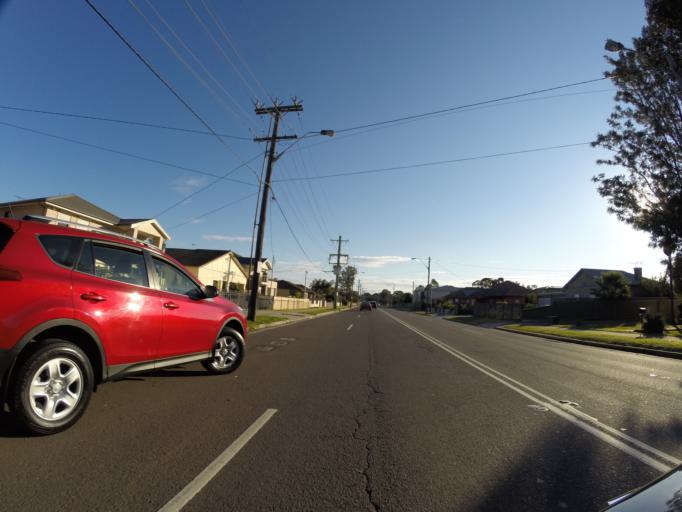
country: AU
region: New South Wales
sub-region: Fairfield
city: Fairfield East
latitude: -33.8685
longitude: 150.9691
